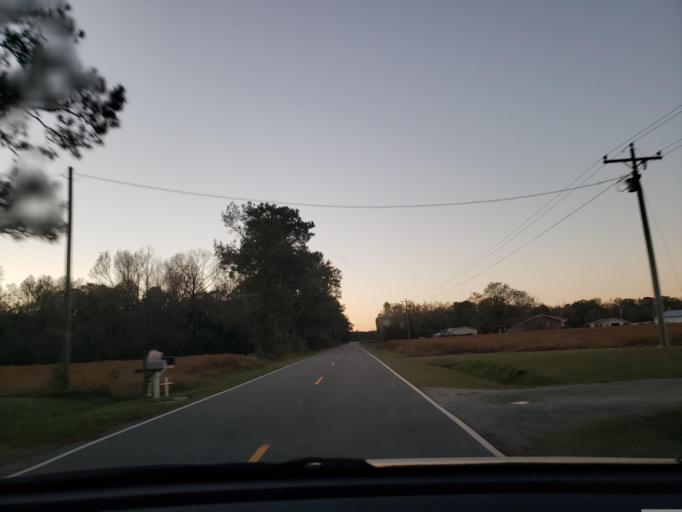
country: US
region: North Carolina
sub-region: Duplin County
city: Beulaville
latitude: 34.7741
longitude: -77.7448
